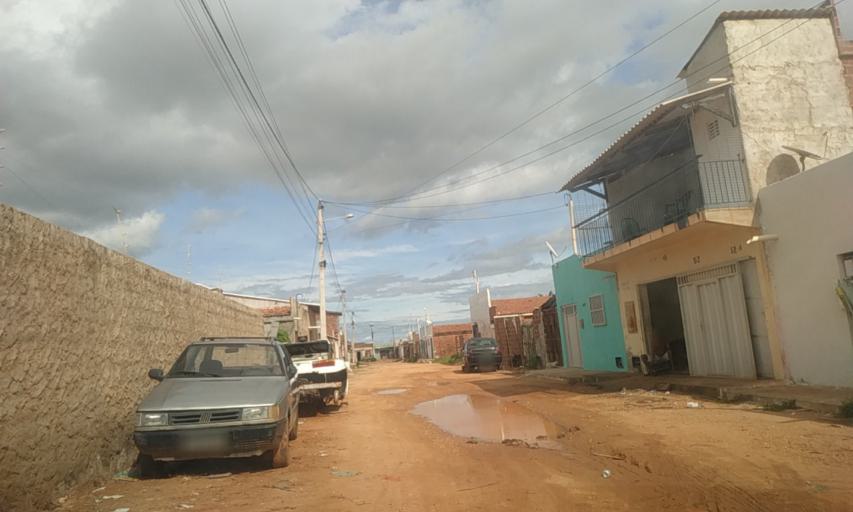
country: BR
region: Rio Grande do Norte
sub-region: Areia Branca
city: Areia Branca
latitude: -4.9523
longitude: -37.1213
